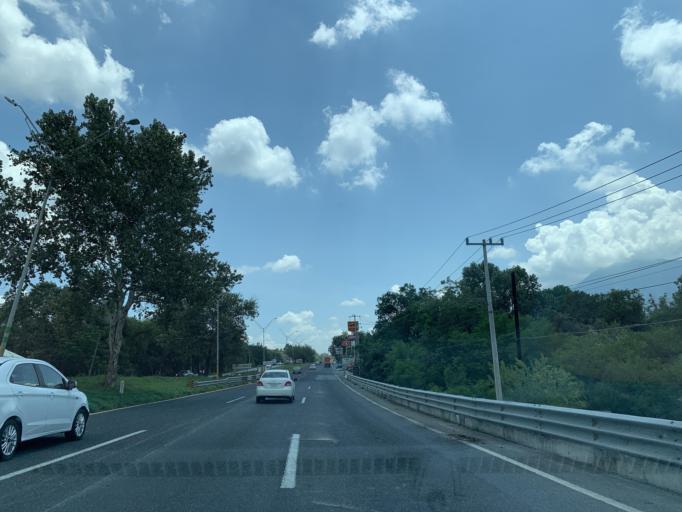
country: MX
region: Nuevo Leon
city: Santiago
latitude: 25.3818
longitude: -100.1136
